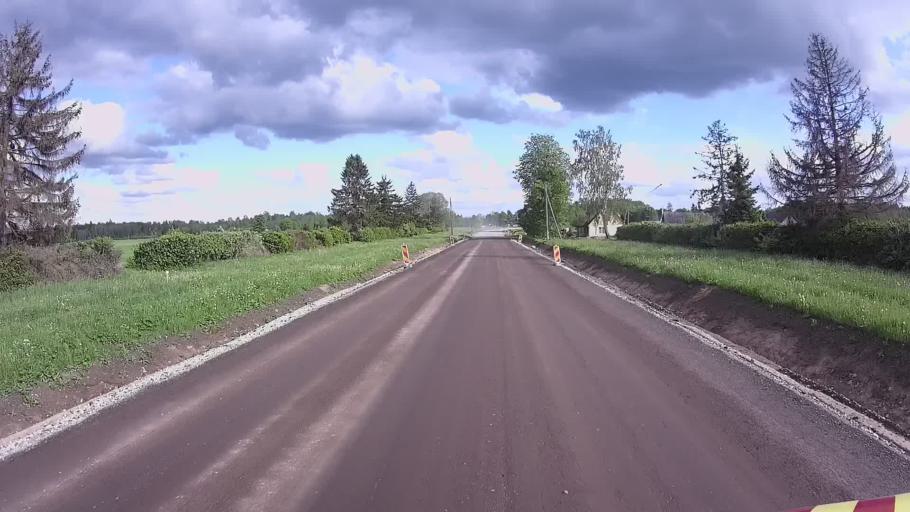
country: EE
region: Jogevamaa
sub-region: Mustvee linn
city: Mustvee
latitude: 59.0202
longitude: 26.7028
